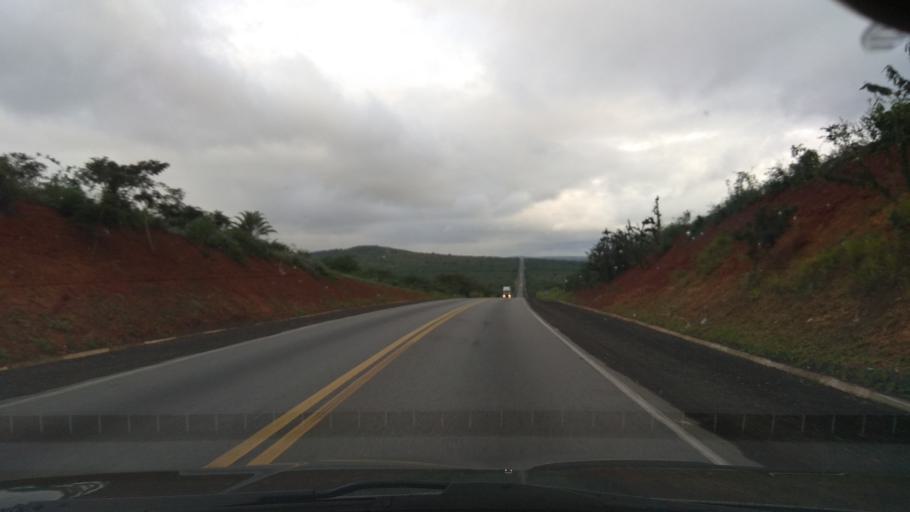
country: BR
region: Bahia
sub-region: Jaguaquara
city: Jaguaquara
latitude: -13.3533
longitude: -40.0166
